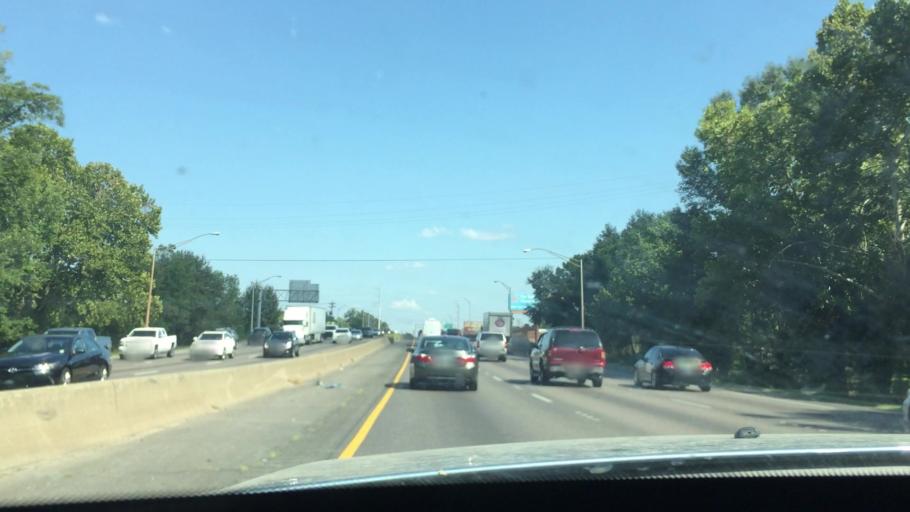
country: US
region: Louisiana
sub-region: East Baton Rouge Parish
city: Baton Rouge
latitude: 30.4253
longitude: -91.1618
